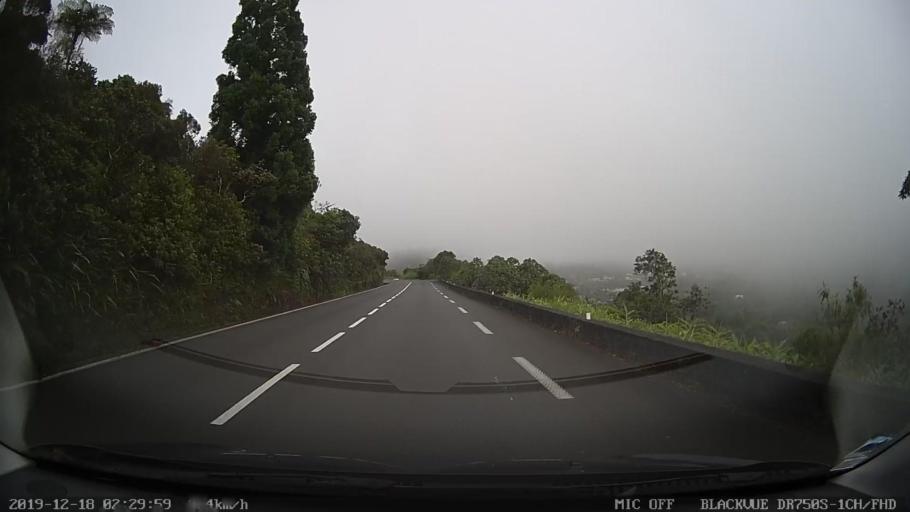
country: RE
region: Reunion
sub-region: Reunion
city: Cilaos
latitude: -21.1559
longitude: 55.6010
